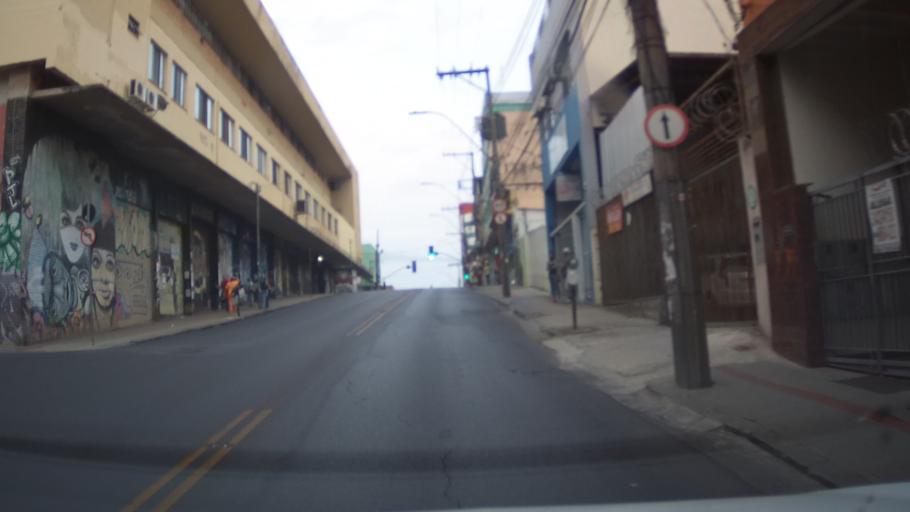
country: BR
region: Minas Gerais
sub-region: Belo Horizonte
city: Belo Horizonte
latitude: -19.9031
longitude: -43.9328
